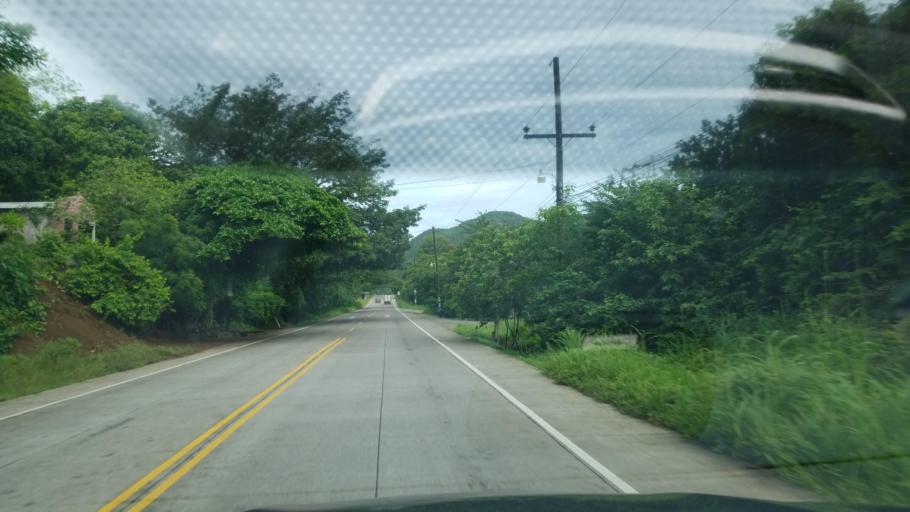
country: HN
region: Francisco Morazan
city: El Porvenir
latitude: 13.6859
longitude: -87.3379
